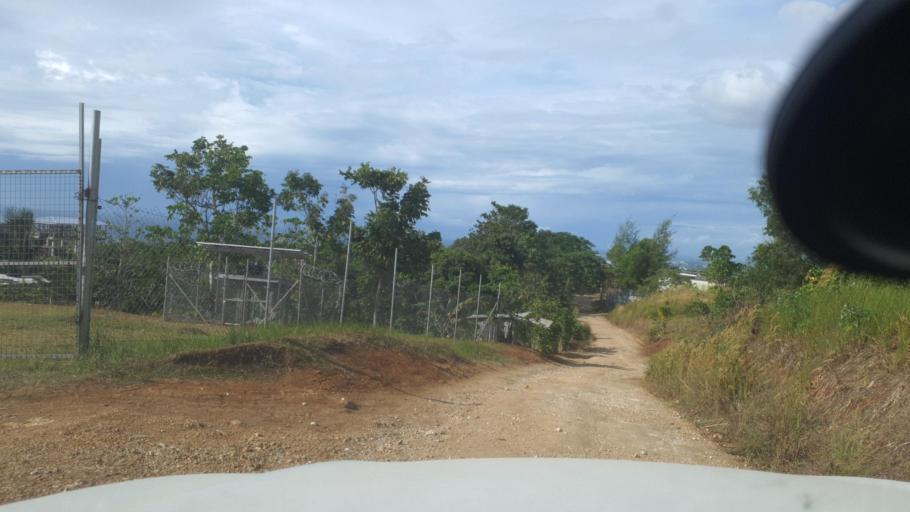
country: SB
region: Guadalcanal
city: Honiara
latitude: -9.4450
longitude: 159.9357
